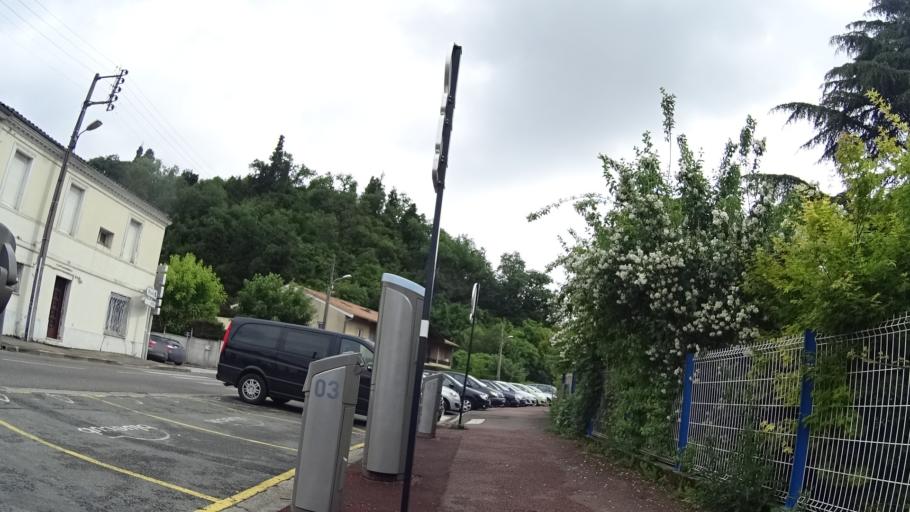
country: FR
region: Aquitaine
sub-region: Departement de la Gironde
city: Floirac
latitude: 44.8307
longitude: -0.5264
